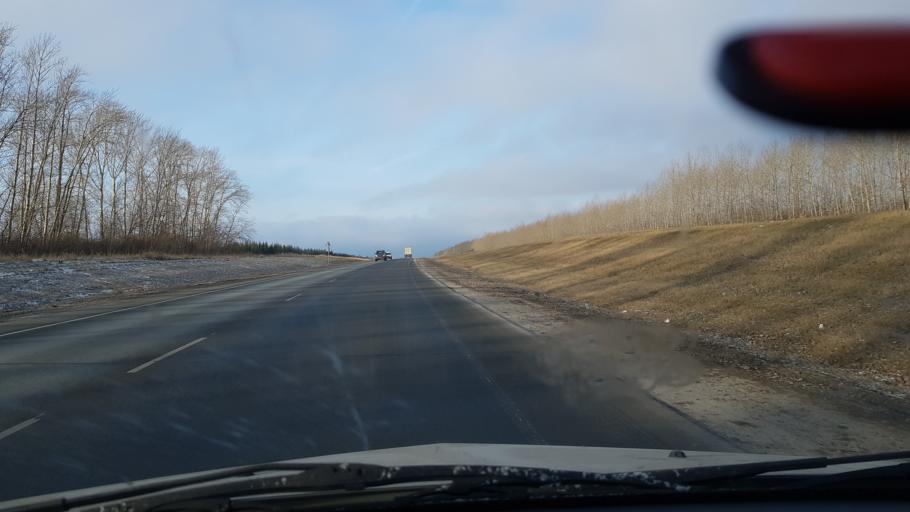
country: RU
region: Tatarstan
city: Laishevo
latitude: 55.3919
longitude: 49.7906
